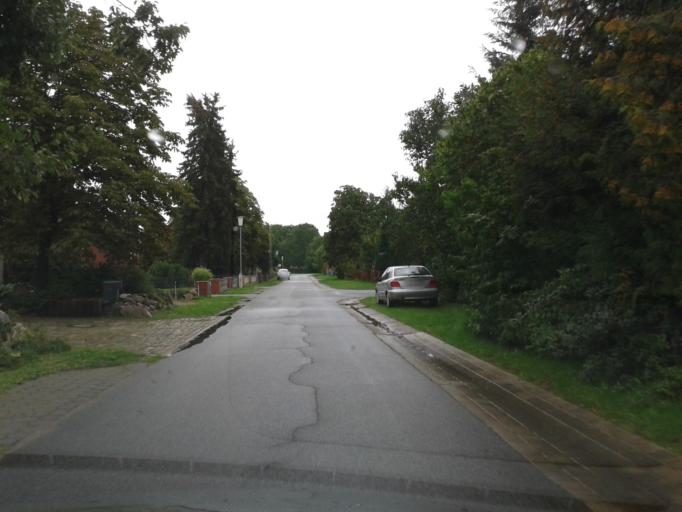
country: DE
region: Lower Saxony
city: Lubbow
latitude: 52.9368
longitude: 11.1864
